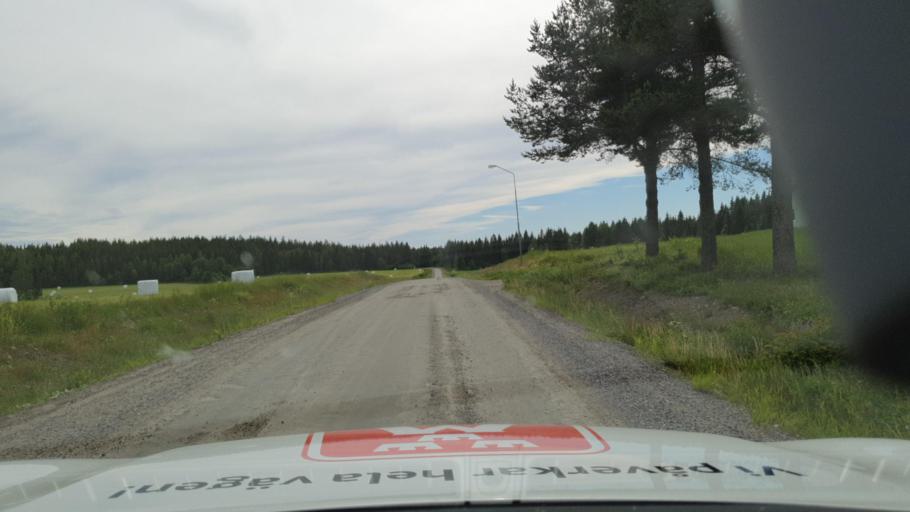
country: SE
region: Vaesterbotten
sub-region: Skelleftea Kommun
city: Burea
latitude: 64.4611
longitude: 21.0381
